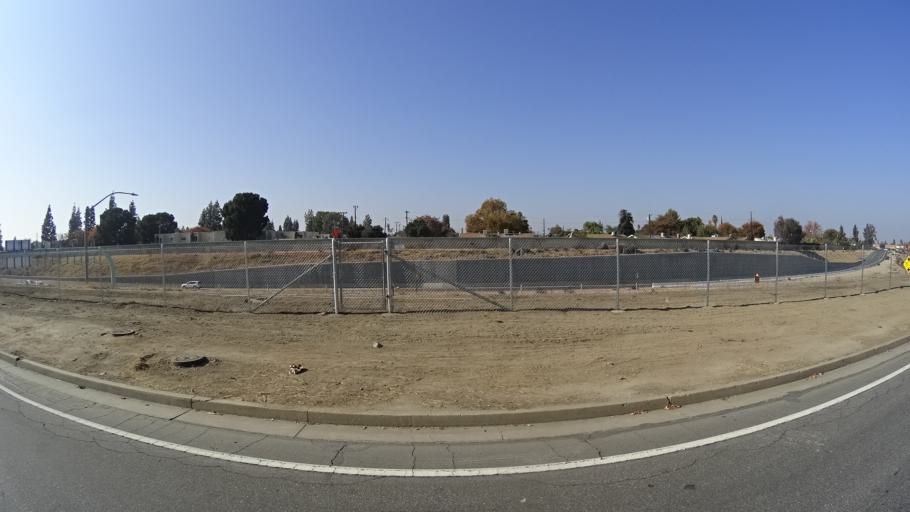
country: US
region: California
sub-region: Kern County
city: Bakersfield
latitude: 35.3360
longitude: -119.0389
